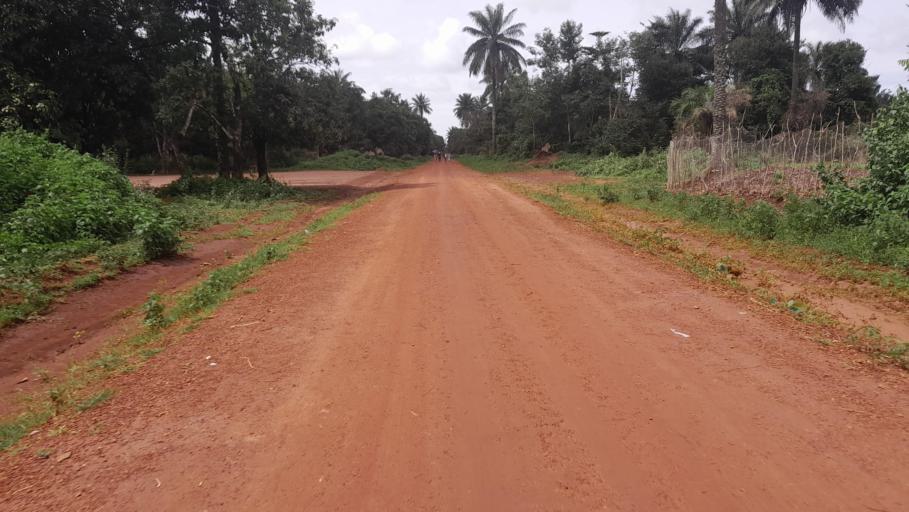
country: GN
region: Boke
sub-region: Boffa
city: Boffa
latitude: 10.0139
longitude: -13.8879
